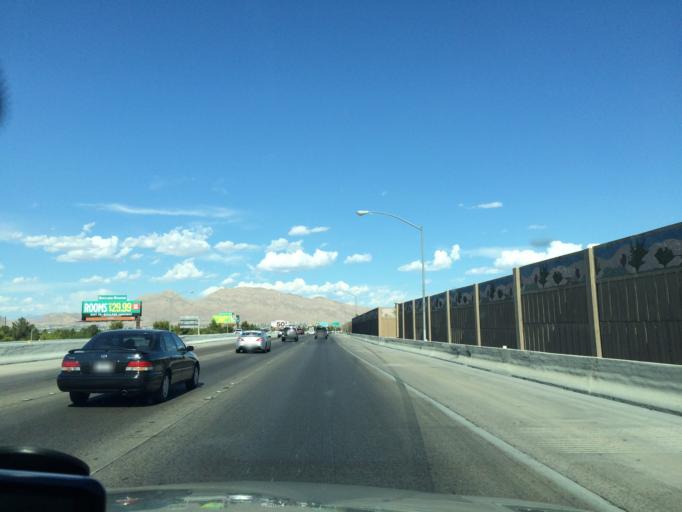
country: US
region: Nevada
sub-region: Clark County
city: Las Vegas
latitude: 36.1676
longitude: -115.1068
